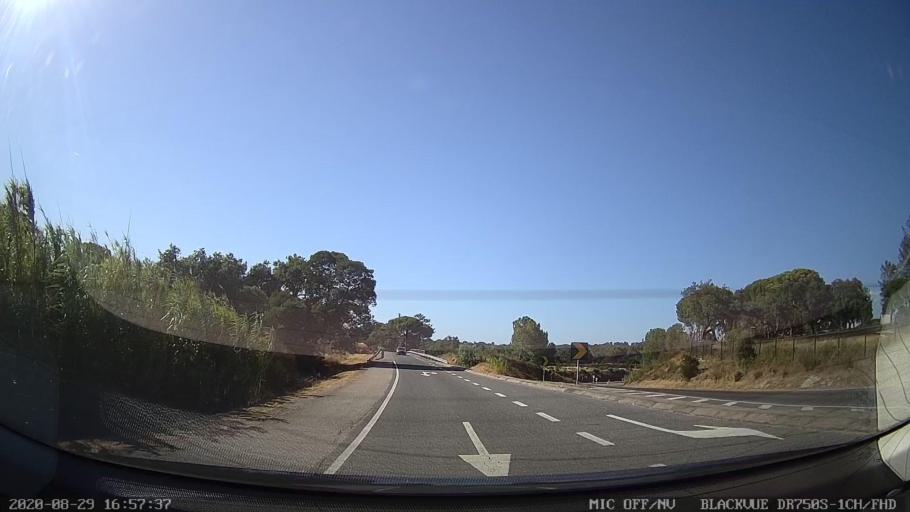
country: PT
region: Setubal
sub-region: Alcacer do Sal
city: Alcacer do Sal
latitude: 38.4026
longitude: -8.5158
